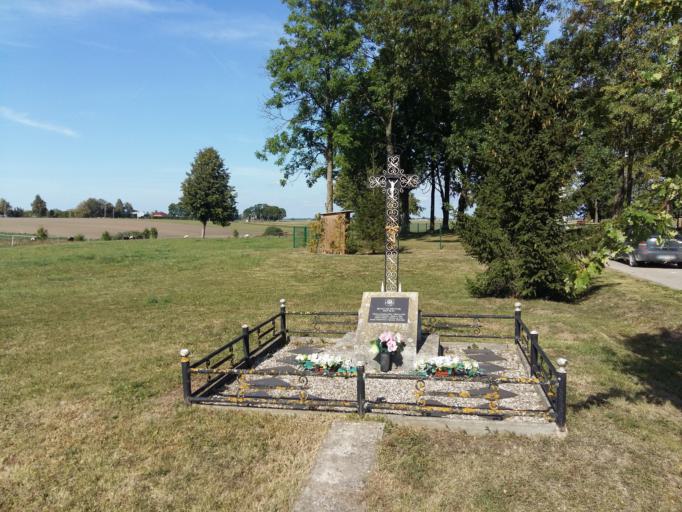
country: LT
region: Marijampoles apskritis
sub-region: Marijampole Municipality
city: Marijampole
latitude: 54.5230
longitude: 23.2640
